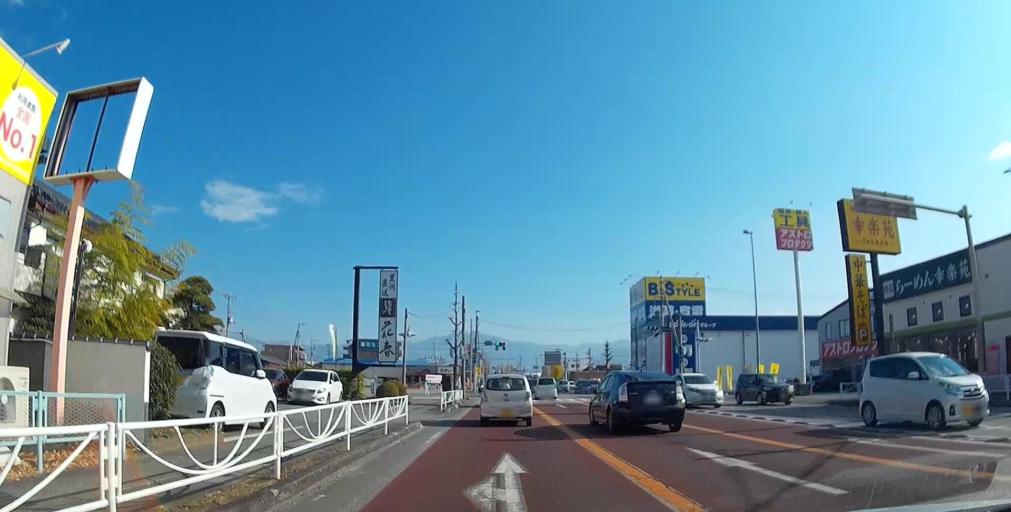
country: JP
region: Yamanashi
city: Isawa
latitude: 35.6456
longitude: 138.6148
